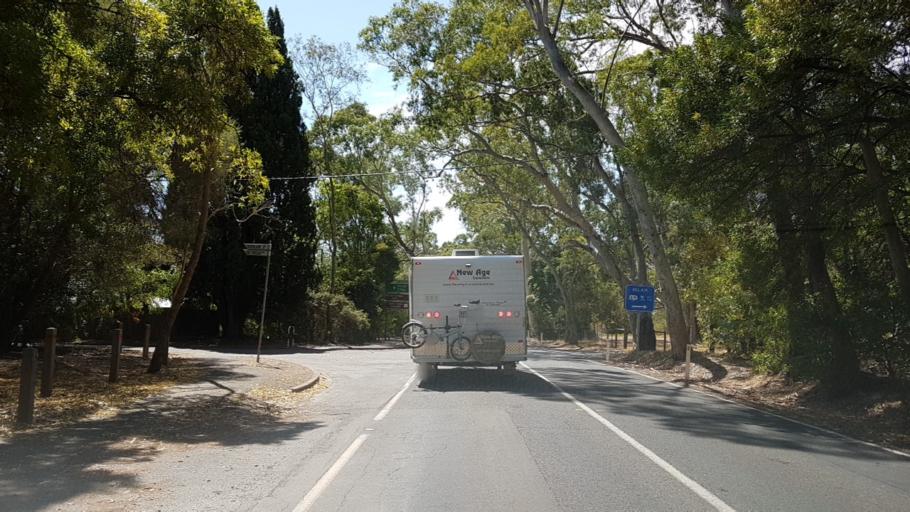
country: AU
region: South Australia
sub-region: Mitcham
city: Belair
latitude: -35.0095
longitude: 138.6332
